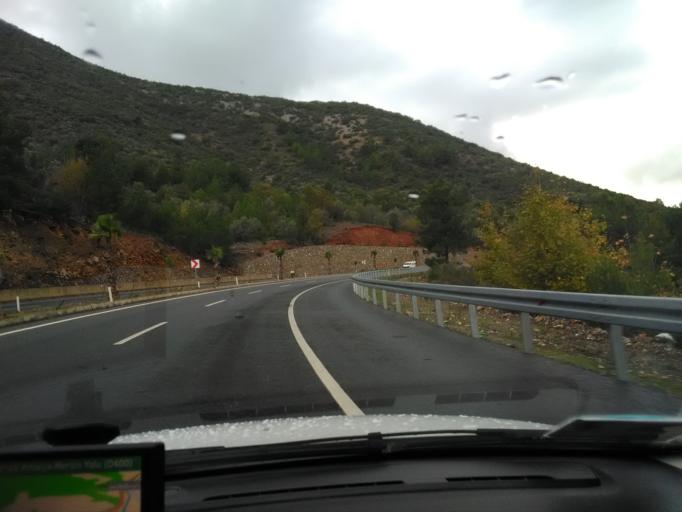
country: TR
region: Antalya
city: Gazipasa
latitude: 36.1770
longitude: 32.4384
